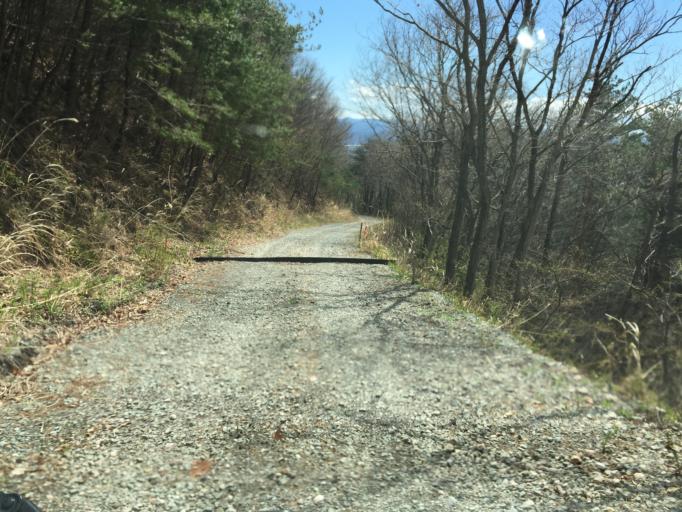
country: JP
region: Fukushima
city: Fukushima-shi
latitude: 37.8505
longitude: 140.4190
